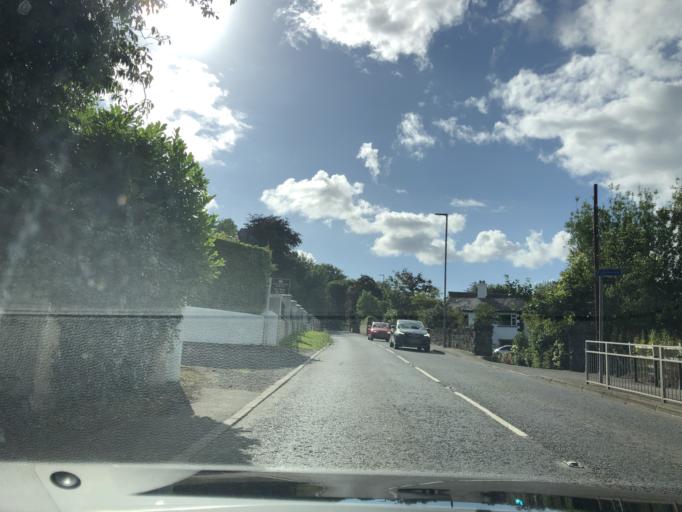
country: GB
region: Northern Ireland
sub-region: Castlereagh District
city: Dundonald
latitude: 54.5862
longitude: -5.8003
